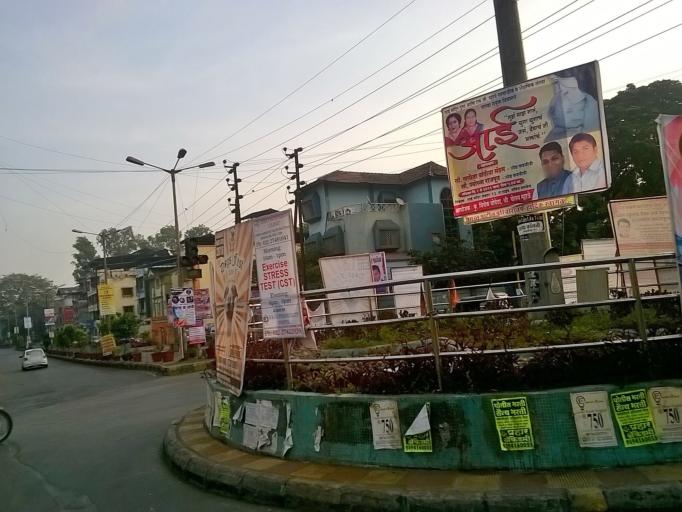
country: IN
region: Maharashtra
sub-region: Raigarh
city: Panvel
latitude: 18.9966
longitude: 73.1190
